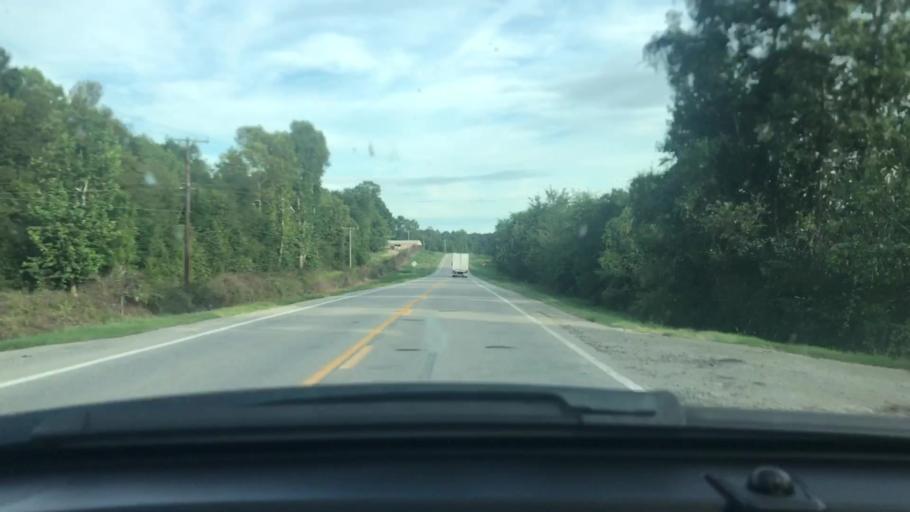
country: US
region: Arkansas
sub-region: Lawrence County
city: Hoxie
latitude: 36.1208
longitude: -91.1483
